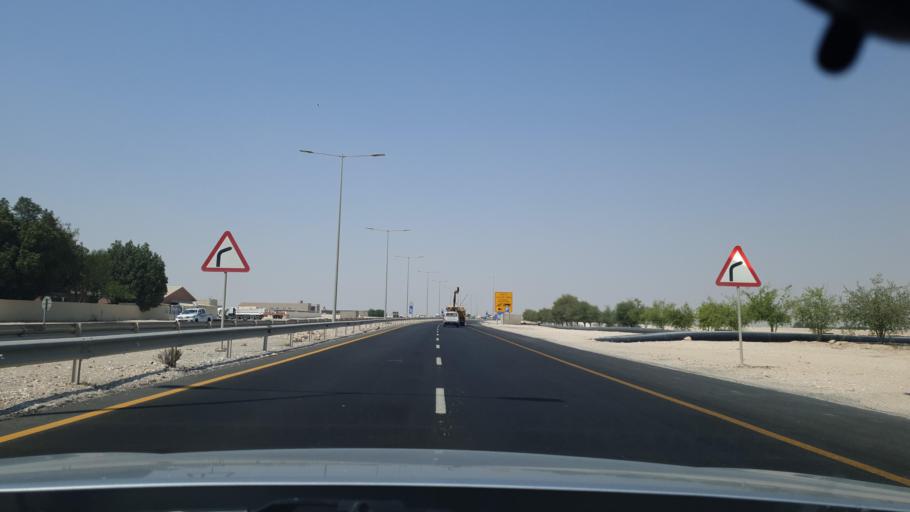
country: QA
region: Al Khawr
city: Al Khawr
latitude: 25.7183
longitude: 51.5031
